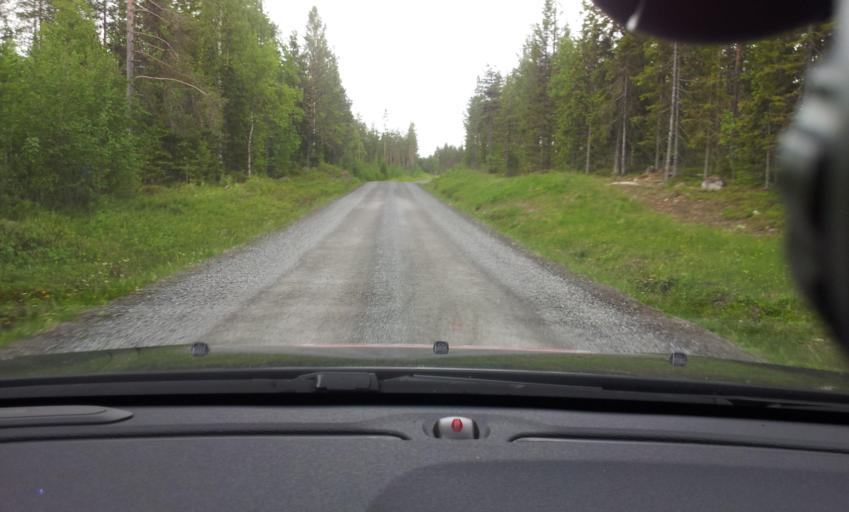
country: SE
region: Jaemtland
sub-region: OEstersunds Kommun
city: Brunflo
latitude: 63.1360
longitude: 15.0685
